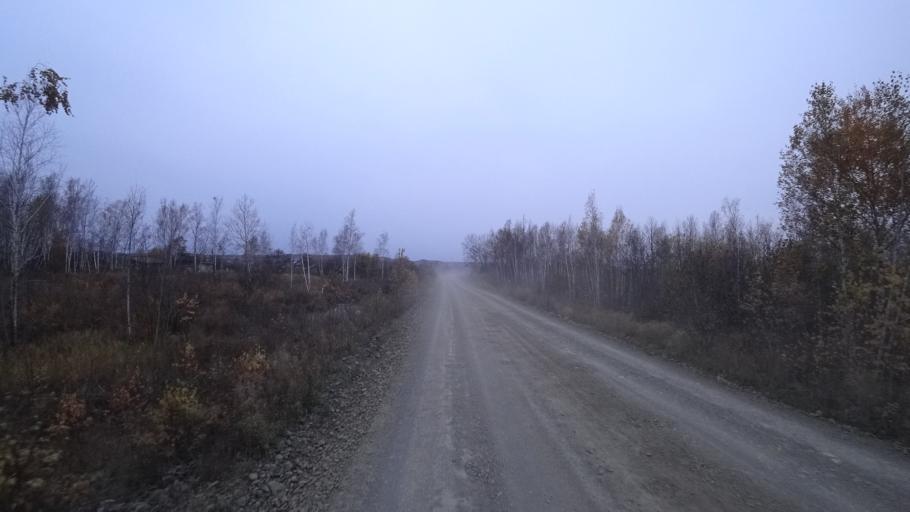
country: RU
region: Khabarovsk Krai
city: Amursk
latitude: 49.8957
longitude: 136.1487
